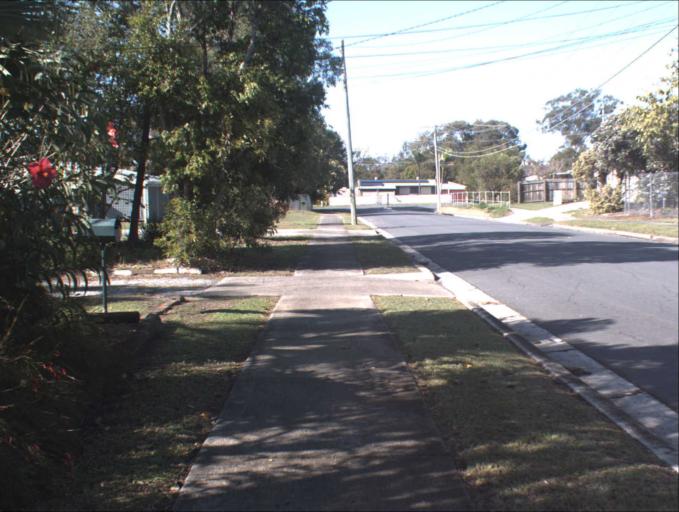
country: AU
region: Queensland
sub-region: Logan
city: Waterford West
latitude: -27.6752
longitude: 153.1031
